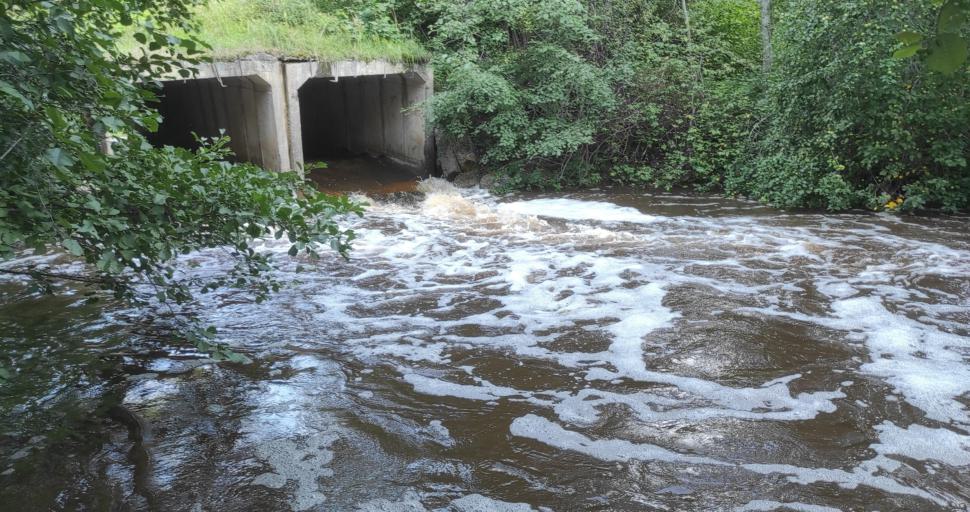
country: LV
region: Kuldigas Rajons
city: Kuldiga
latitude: 56.9880
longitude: 22.0483
